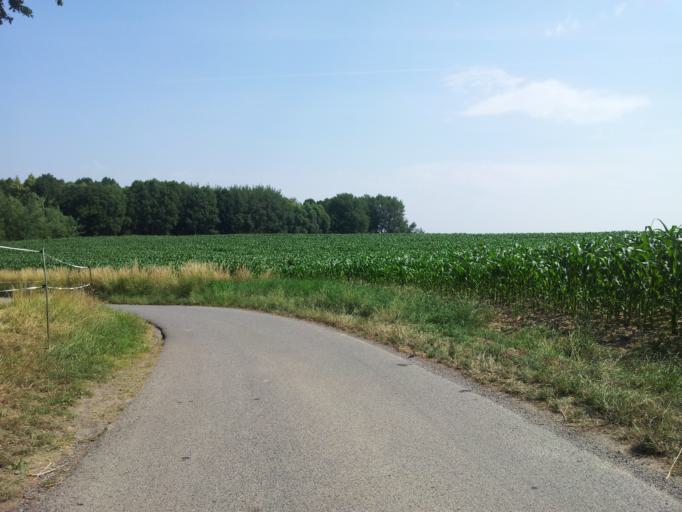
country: DE
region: Saxony
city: Panschwitz-Kuckau
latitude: 51.2184
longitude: 14.2050
